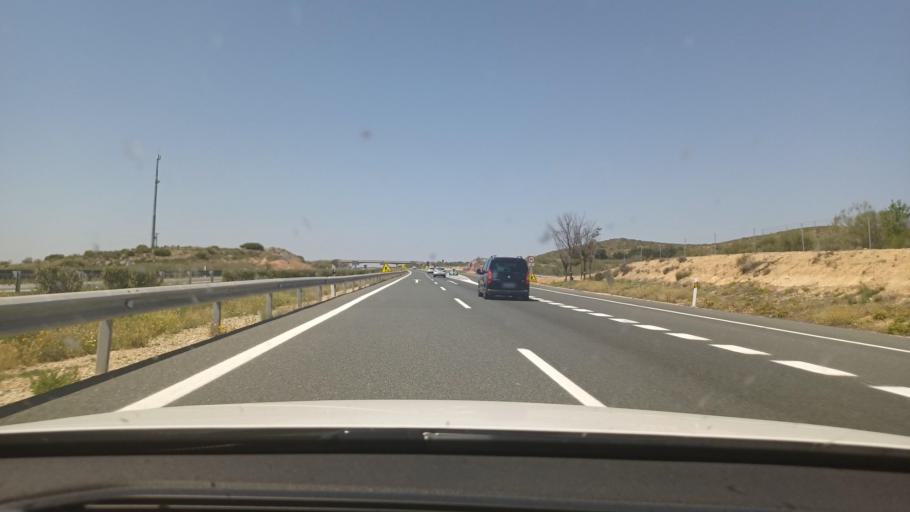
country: ES
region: Castille-La Mancha
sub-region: Provincia de Albacete
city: Almansa
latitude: 38.8788
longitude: -1.1674
